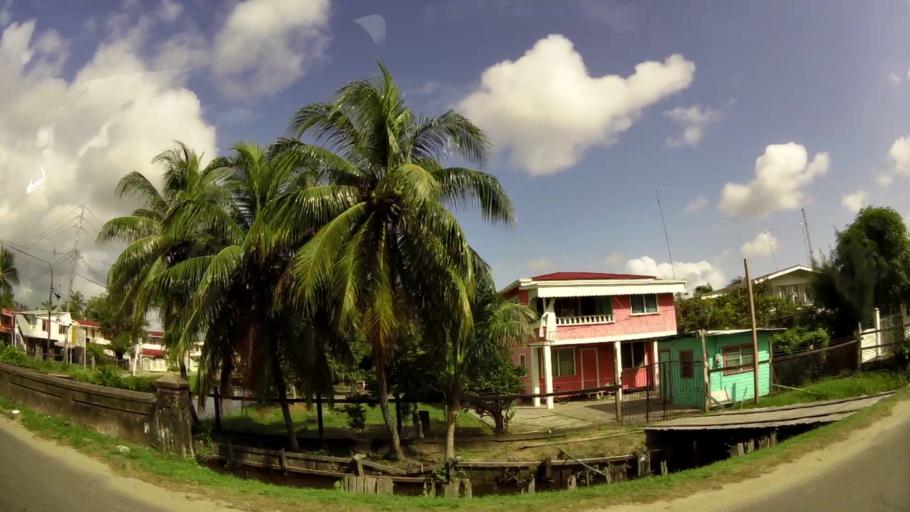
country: GY
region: Demerara-Mahaica
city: Mahaica Village
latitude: 6.6734
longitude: -57.9212
